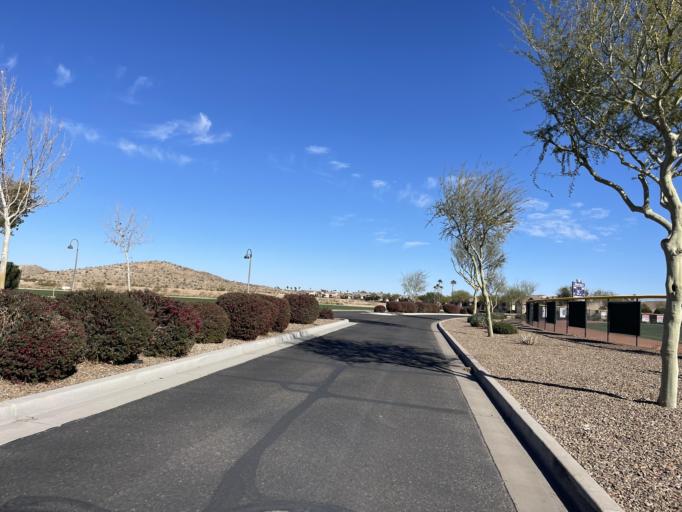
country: US
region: Arizona
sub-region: Pinal County
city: Arizona City
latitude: 32.8177
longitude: -111.6385
